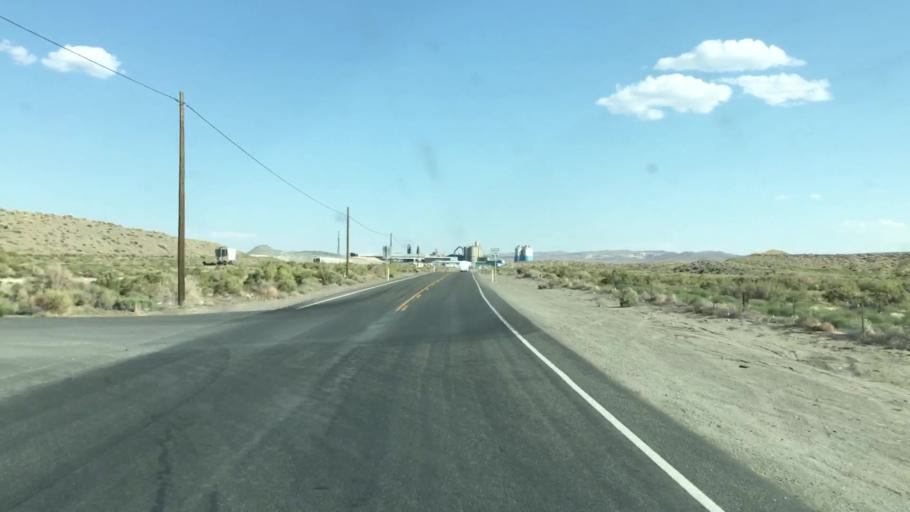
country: US
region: Nevada
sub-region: Lyon County
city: Fernley
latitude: 39.6290
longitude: -119.2754
